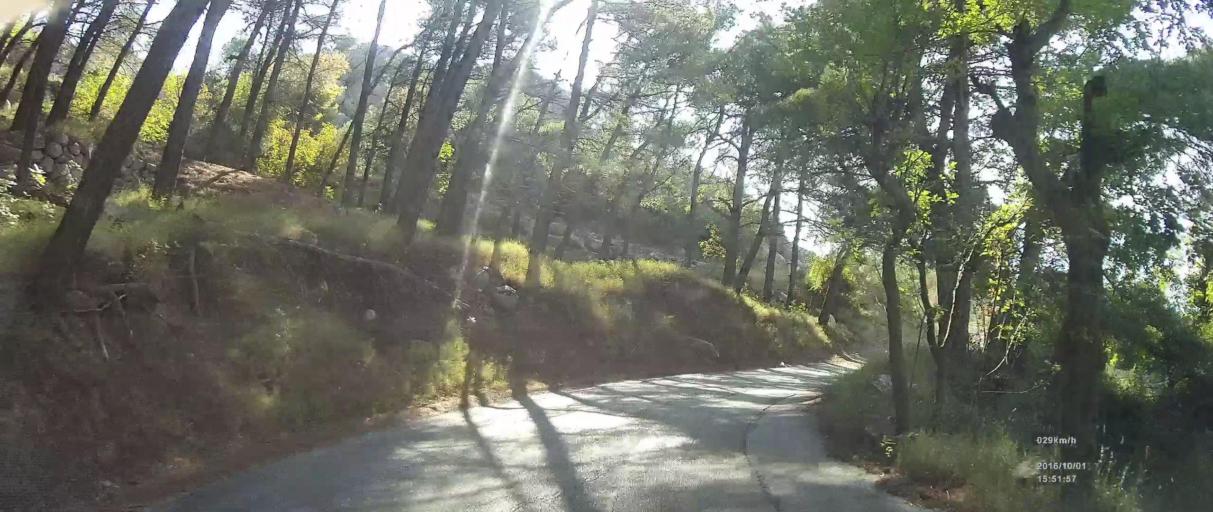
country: HR
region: Splitsko-Dalmatinska
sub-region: Grad Omis
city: Omis
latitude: 43.4364
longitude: 16.7057
